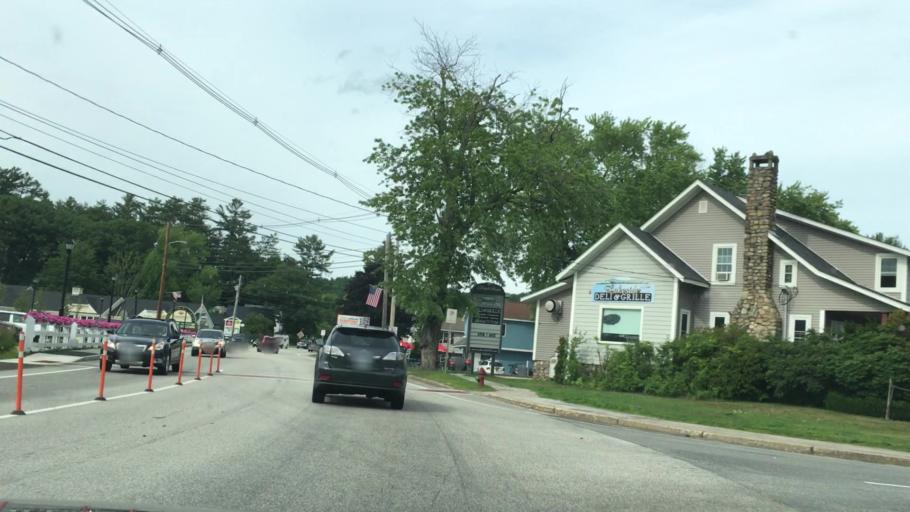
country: US
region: New Hampshire
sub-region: Belknap County
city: Meredith
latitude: 43.6595
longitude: -71.4972
